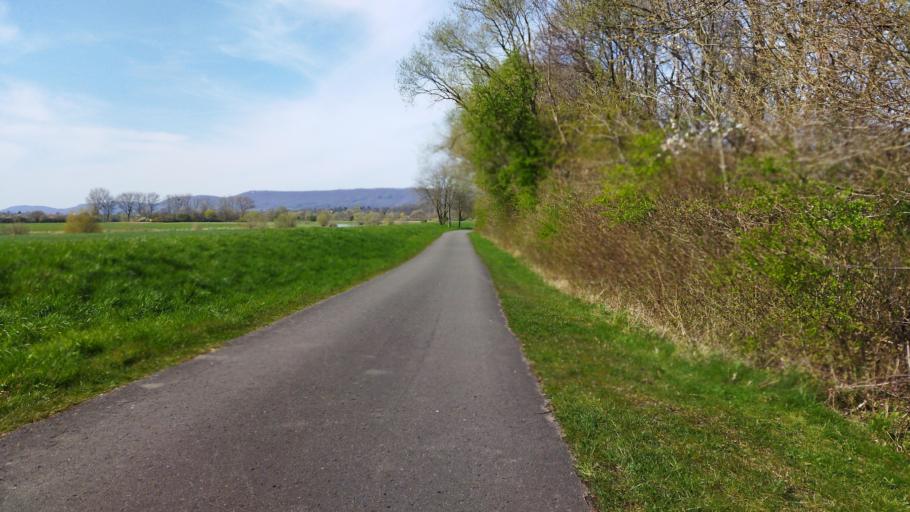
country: DE
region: Lower Saxony
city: Hessisch Oldendorf
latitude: 52.1562
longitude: 9.2708
